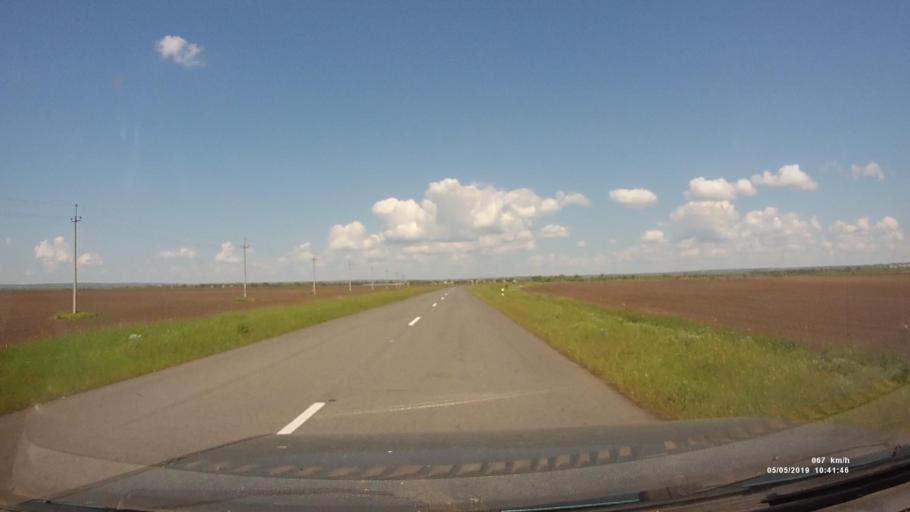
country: RU
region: Rostov
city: Ust'-Donetskiy
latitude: 47.5934
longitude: 40.8394
